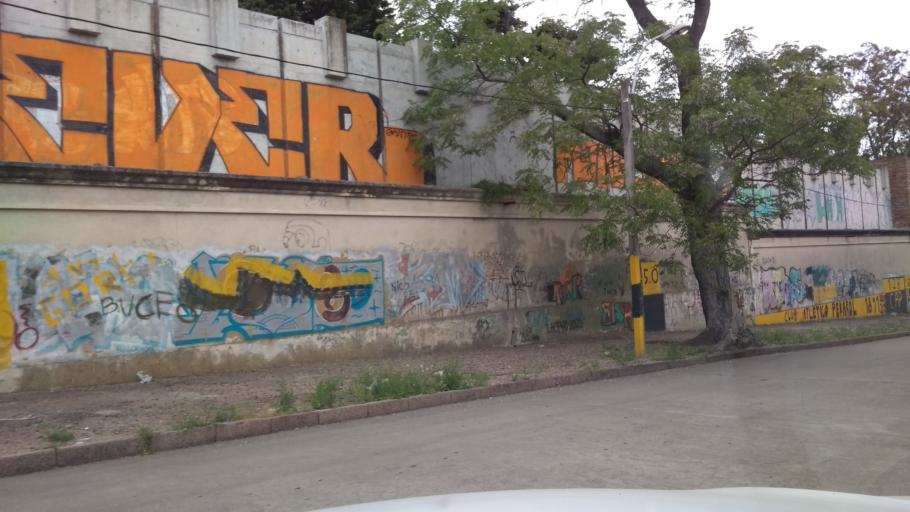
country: UY
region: Montevideo
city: Montevideo
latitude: -34.9035
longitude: -56.1261
